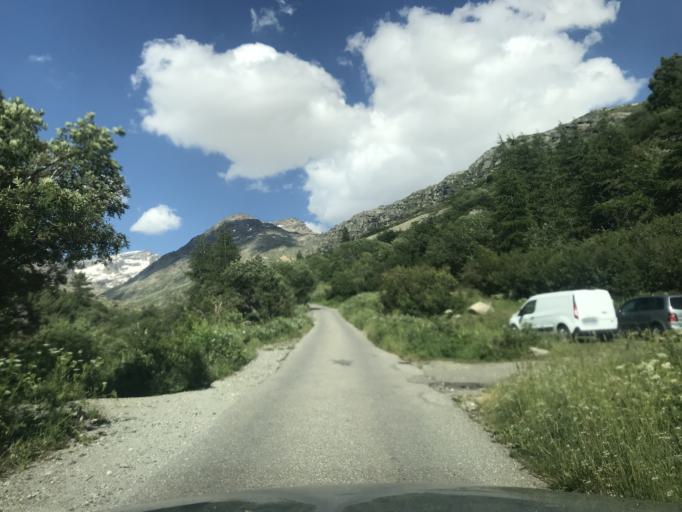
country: FR
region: Rhone-Alpes
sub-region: Departement de la Savoie
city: Val-d'Isere
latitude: 45.3758
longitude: 7.0807
